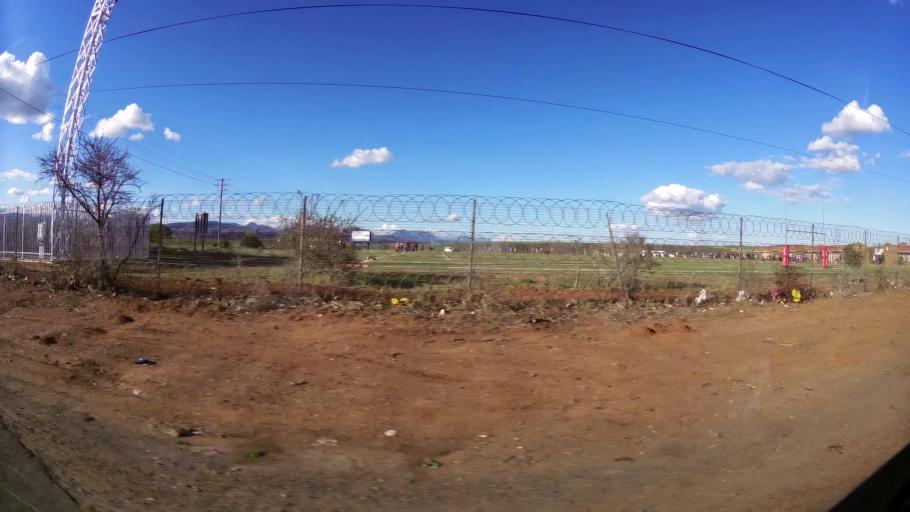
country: ZA
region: Western Cape
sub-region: Eden District Municipality
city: Riversdale
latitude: -34.1057
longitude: 20.9554
